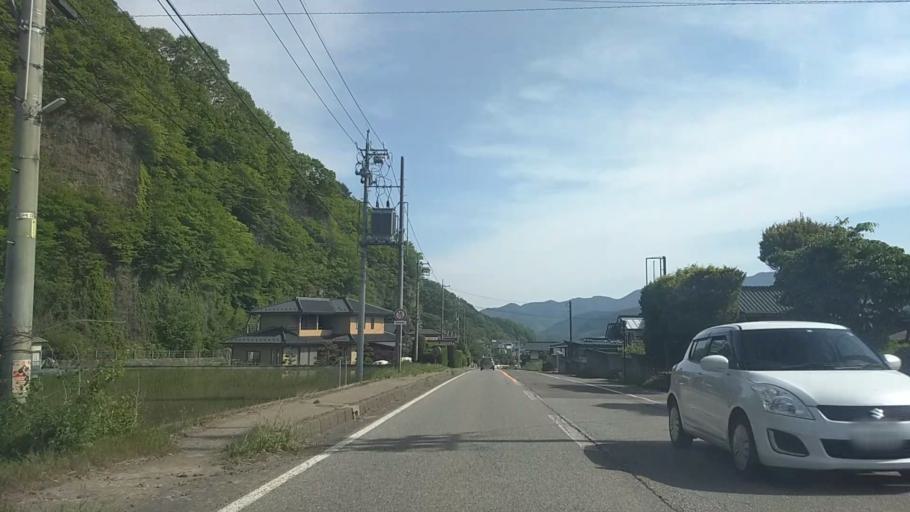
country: JP
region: Nagano
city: Saku
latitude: 36.0714
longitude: 138.4761
